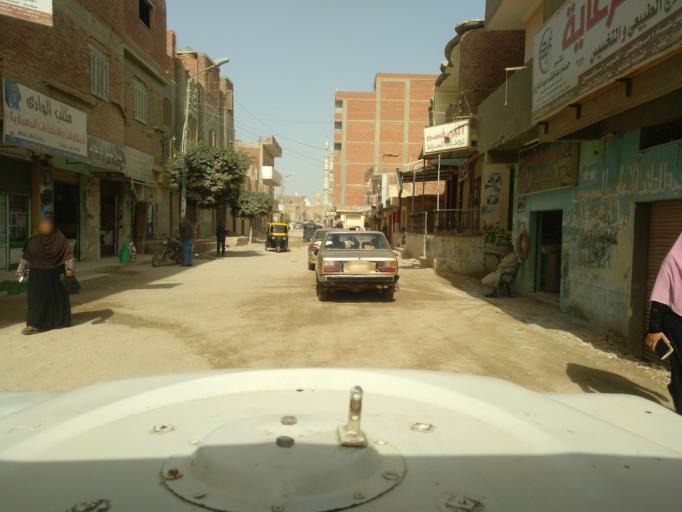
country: EG
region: Al Buhayrah
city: Beheira
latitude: 30.3738
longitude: 30.3513
